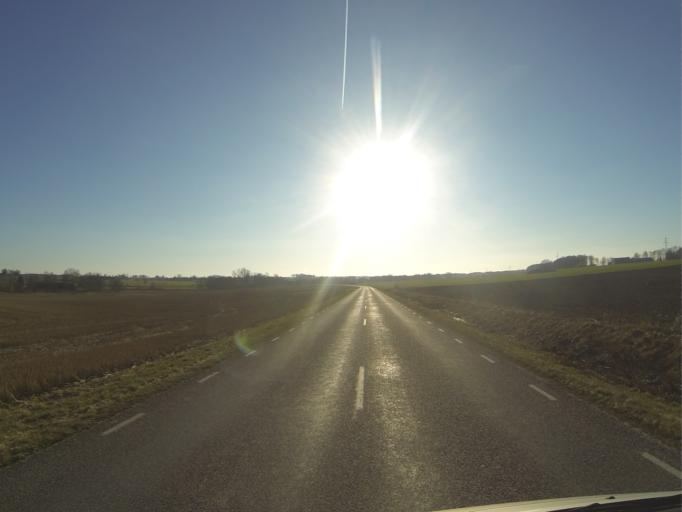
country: SE
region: Skane
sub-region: Hoors Kommun
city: Loberod
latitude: 55.7952
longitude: 13.5468
